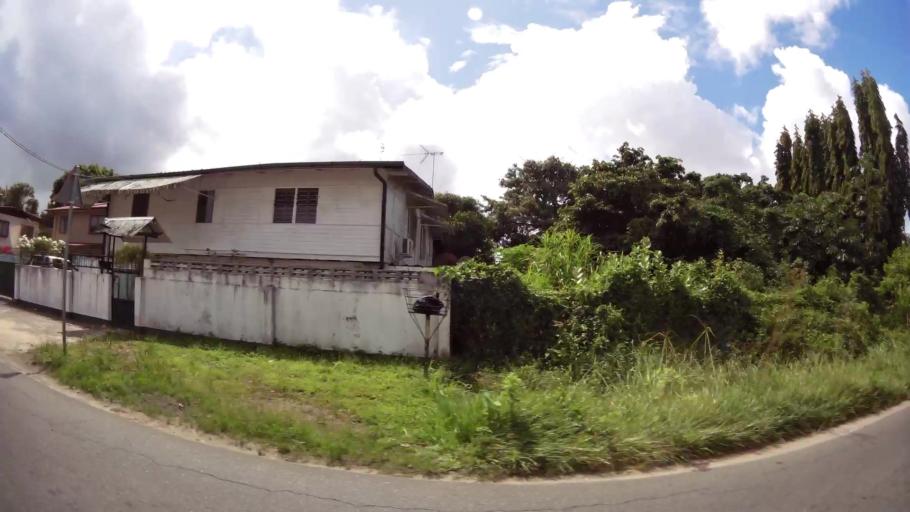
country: SR
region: Paramaribo
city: Paramaribo
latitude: 5.8344
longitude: -55.1926
